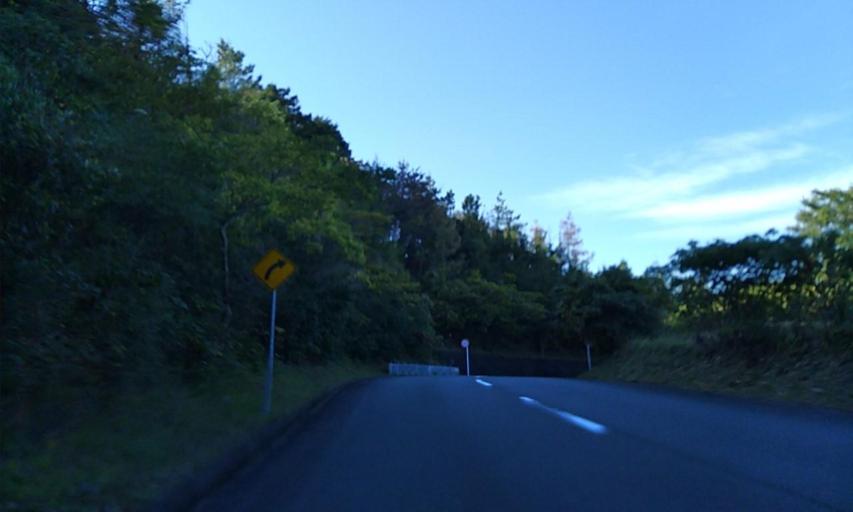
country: JP
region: Shizuoka
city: Hamakita
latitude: 34.8286
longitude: 137.6424
